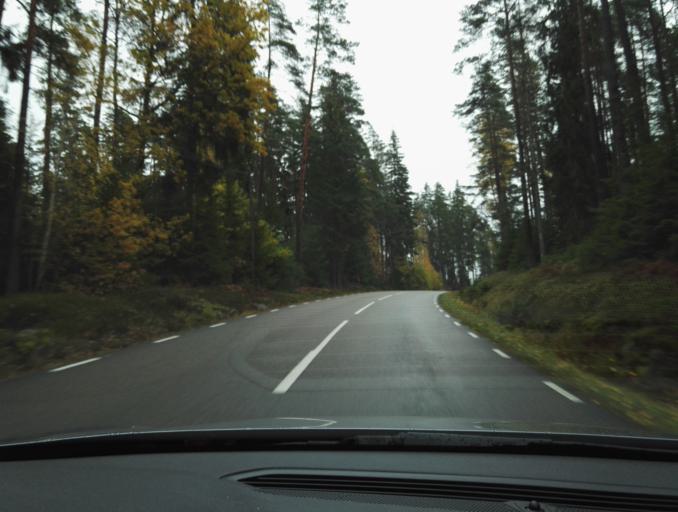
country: SE
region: Kronoberg
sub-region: Vaxjo Kommun
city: Rottne
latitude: 57.0274
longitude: 14.8265
